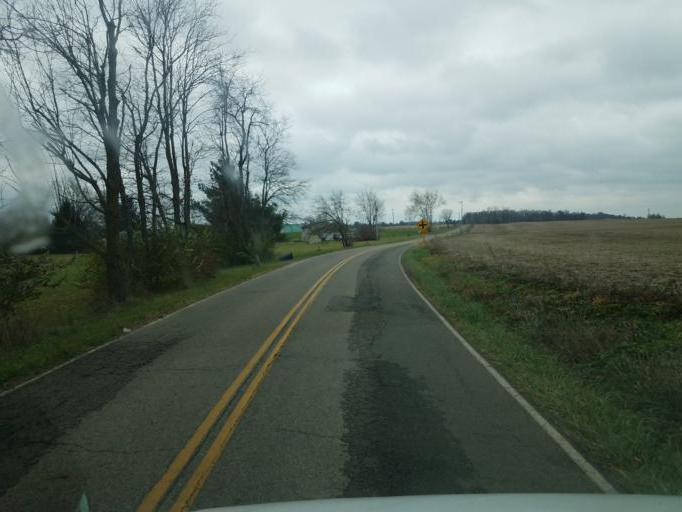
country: US
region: Ohio
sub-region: Licking County
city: Johnstown
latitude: 40.2178
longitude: -82.6520
